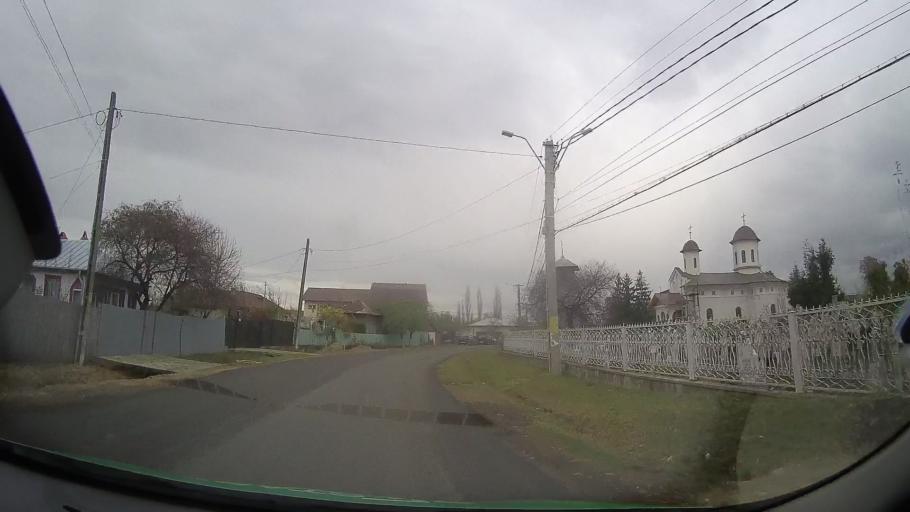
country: RO
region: Prahova
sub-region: Comuna Colceag
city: Inotesti
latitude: 44.9600
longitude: 26.3581
